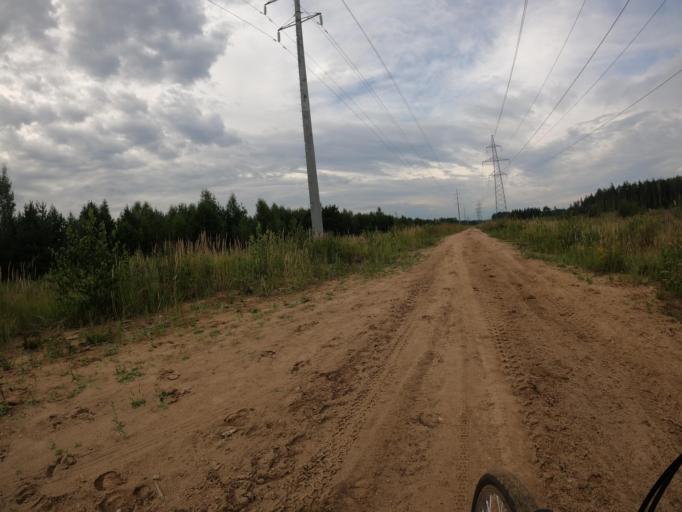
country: RU
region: Moskovskaya
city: Rodniki
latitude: 55.6739
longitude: 38.0832
